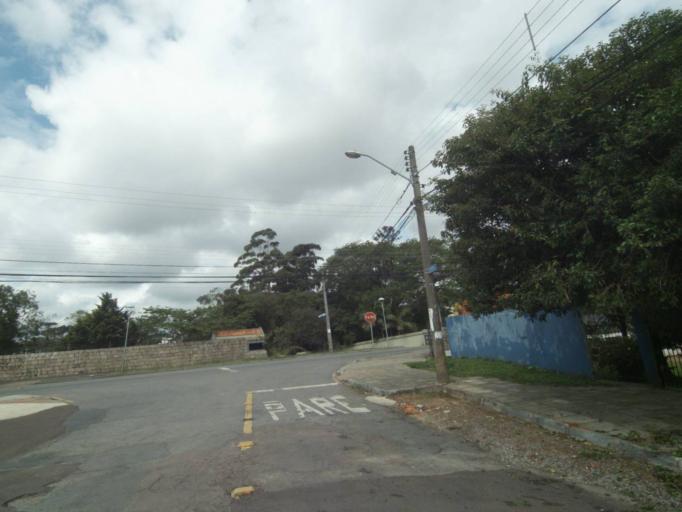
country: BR
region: Parana
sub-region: Curitiba
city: Curitiba
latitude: -25.3852
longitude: -49.2849
